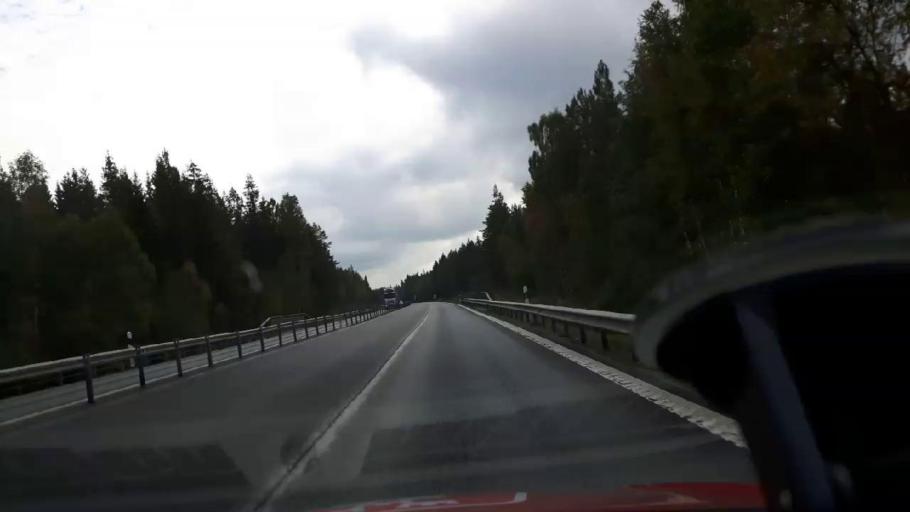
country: SE
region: Gaevleborg
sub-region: Gavle Kommun
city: Norrsundet
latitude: 60.8761
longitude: 17.0479
